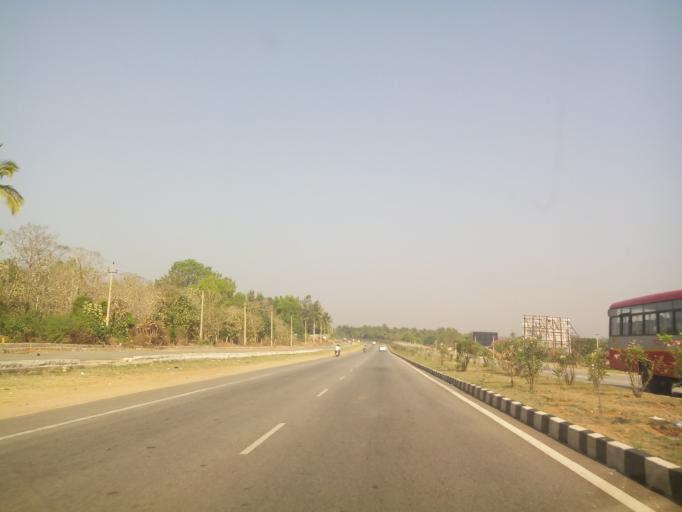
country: IN
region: Karnataka
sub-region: Bangalore Rural
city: Nelamangala
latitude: 13.0643
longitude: 77.3275
